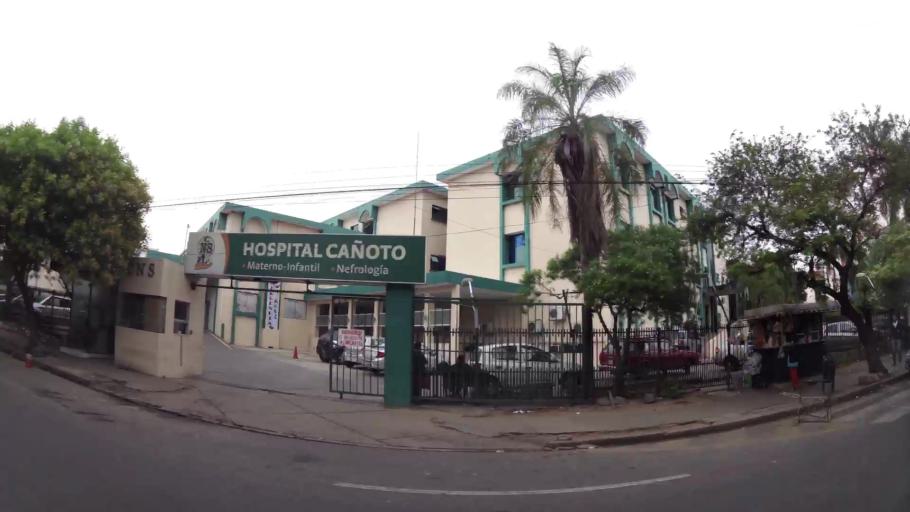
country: BO
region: Santa Cruz
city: Santa Cruz de la Sierra
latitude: -17.7778
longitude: -63.1879
